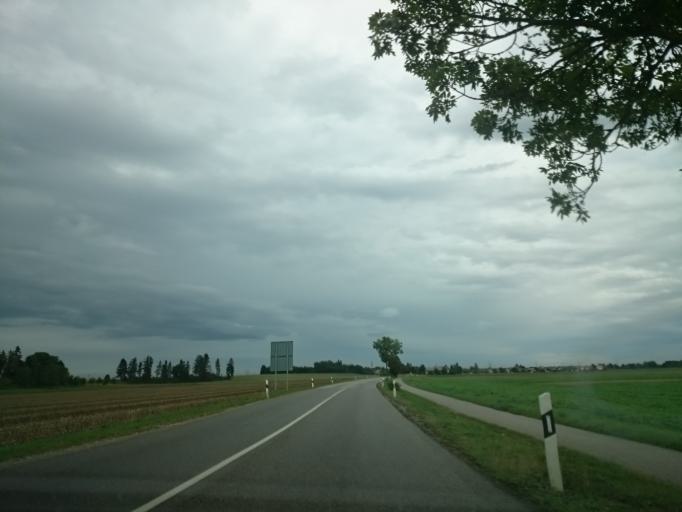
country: DE
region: Bavaria
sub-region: Swabia
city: Kleinaitingen
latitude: 48.2067
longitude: 10.8330
